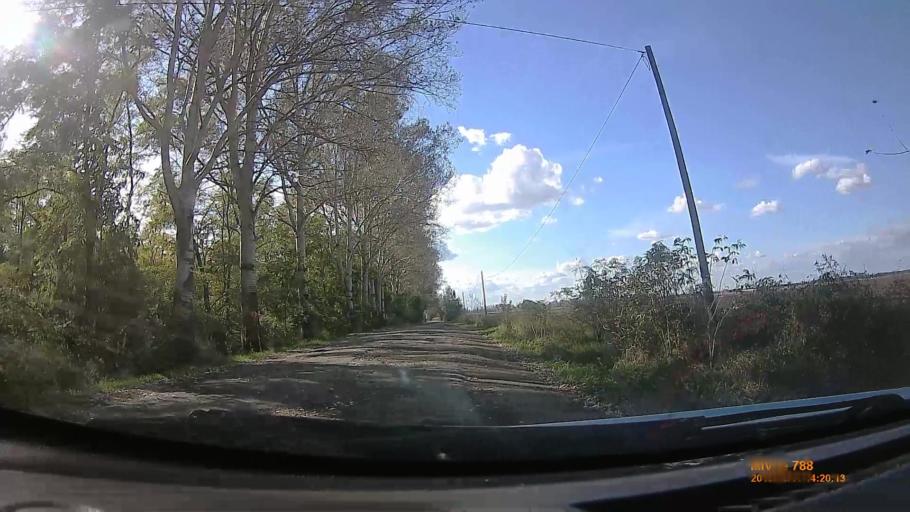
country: HU
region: Hajdu-Bihar
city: Hajduszoboszlo
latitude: 47.5293
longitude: 21.3820
